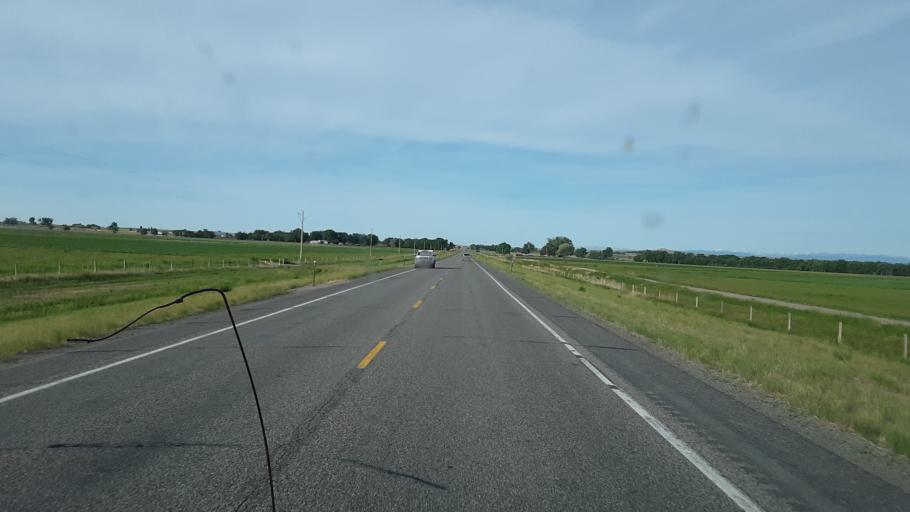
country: US
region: Wyoming
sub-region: Fremont County
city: Riverton
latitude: 43.1952
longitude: -108.2368
